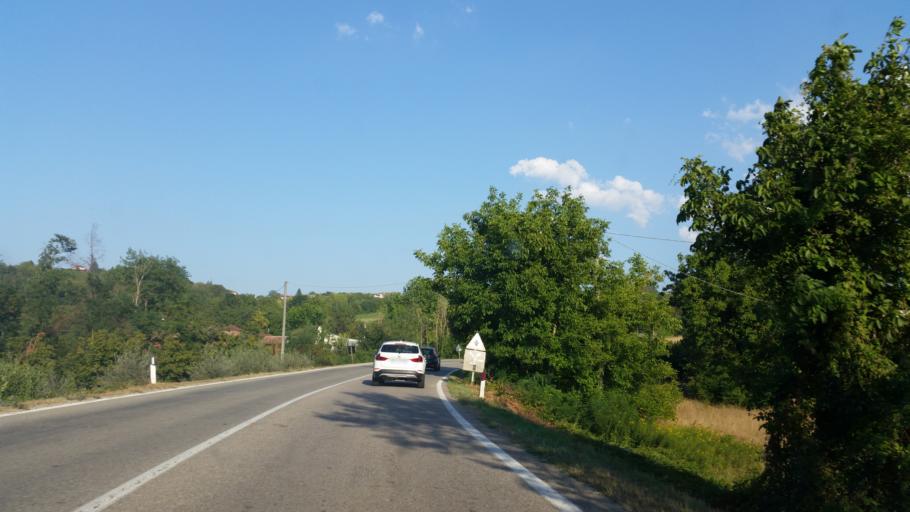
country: IT
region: Piedmont
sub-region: Provincia di Cuneo
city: Barbaresco
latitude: 44.7412
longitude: 8.0902
